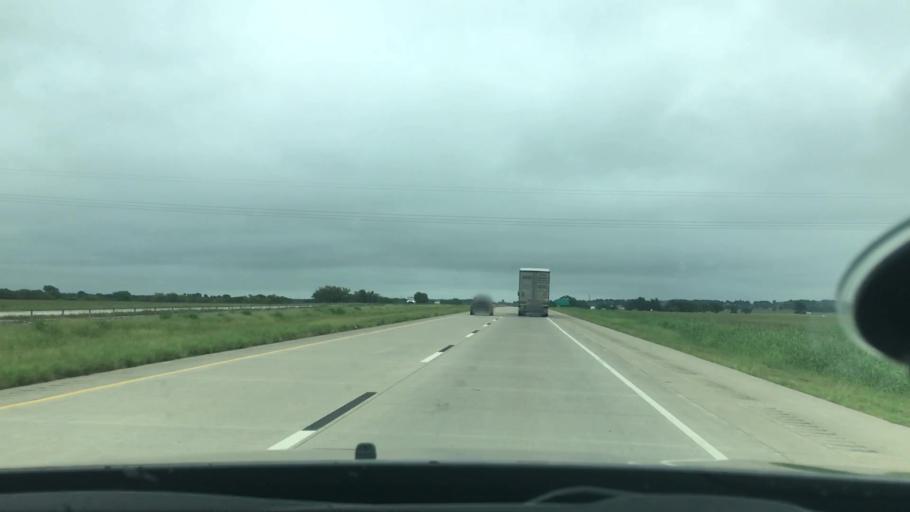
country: US
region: Oklahoma
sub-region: McIntosh County
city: Checotah
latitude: 35.4564
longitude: -95.4766
